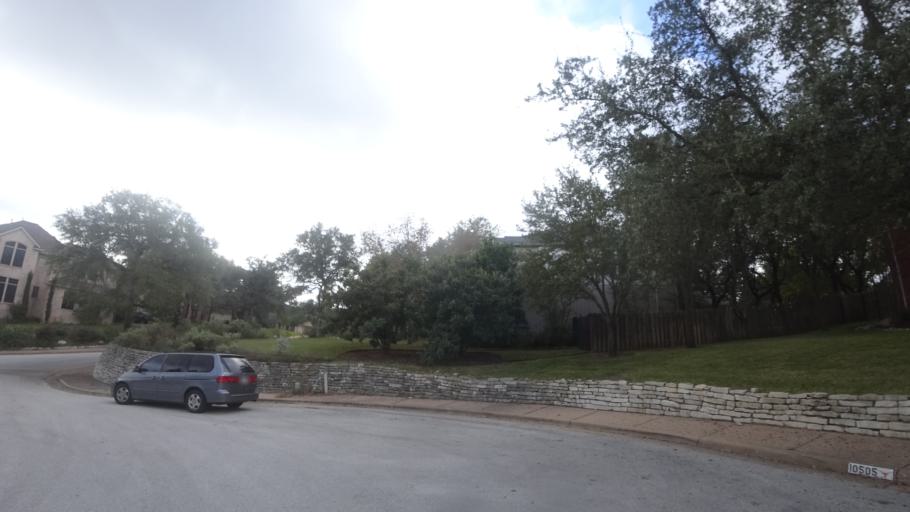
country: US
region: Texas
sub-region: Travis County
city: Barton Creek
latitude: 30.3120
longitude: -97.8973
